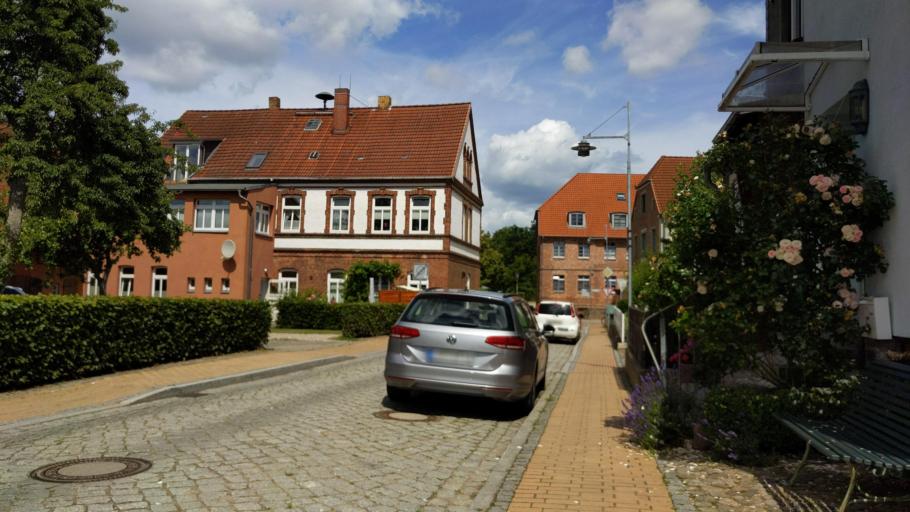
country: DE
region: Mecklenburg-Vorpommern
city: Dassow
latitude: 53.9072
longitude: 10.9753
